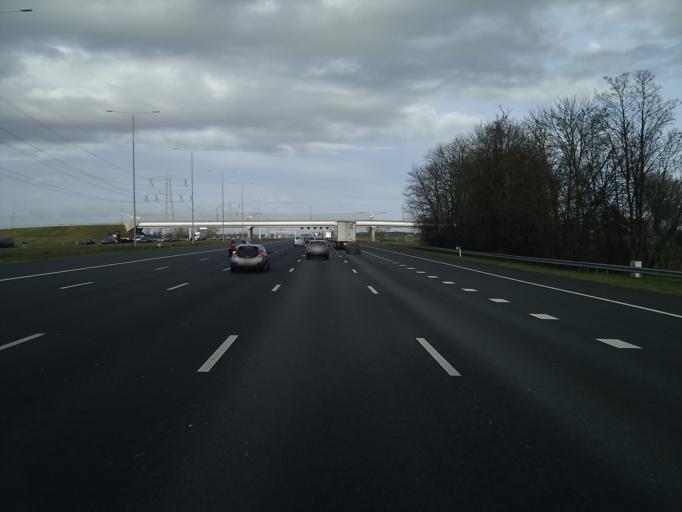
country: NL
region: Utrecht
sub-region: Stichtse Vecht
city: Breukelen
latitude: 52.1876
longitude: 4.9868
